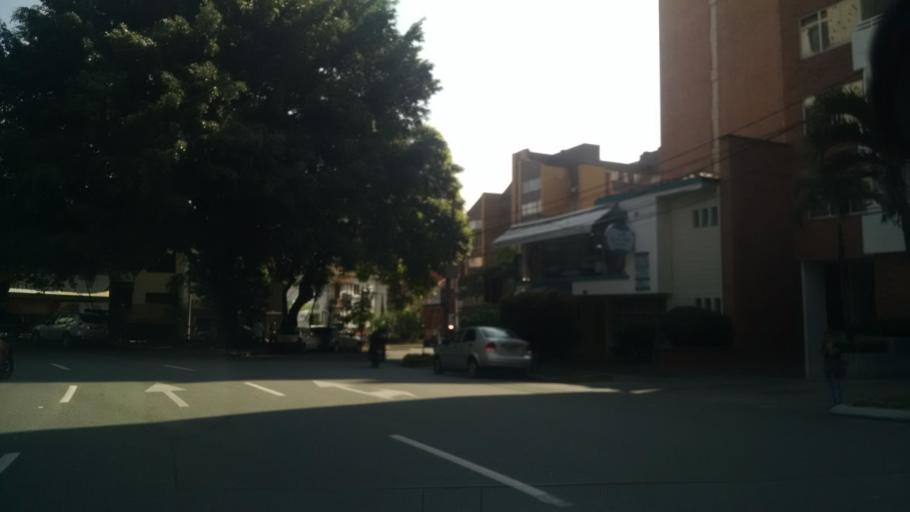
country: CO
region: Antioquia
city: Medellin
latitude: 6.2446
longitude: -75.5969
